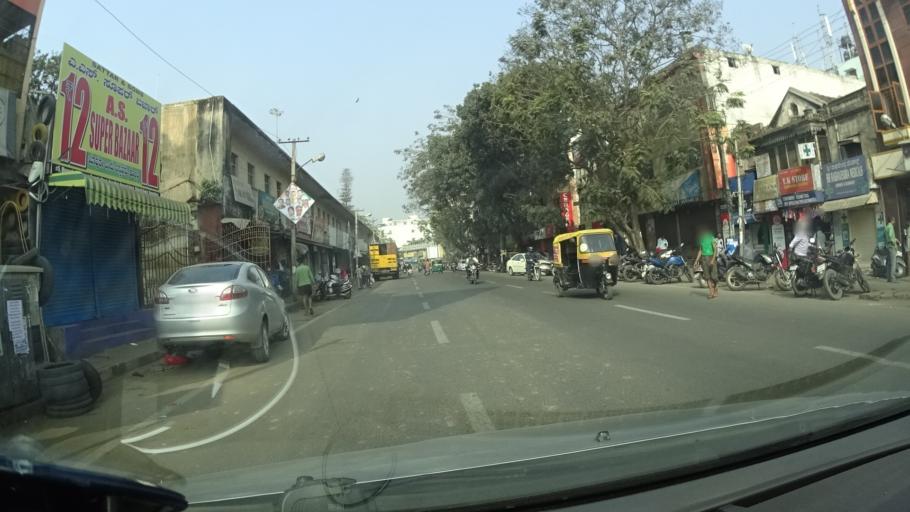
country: IN
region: Karnataka
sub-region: Bangalore Urban
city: Bangalore
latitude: 12.9842
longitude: 77.6030
